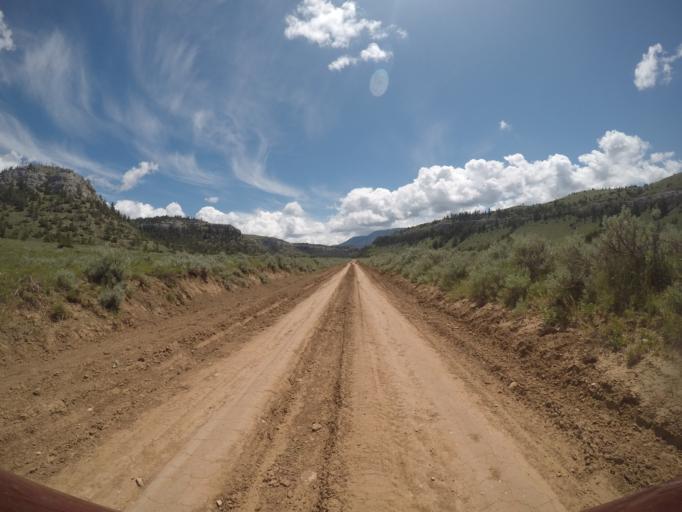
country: US
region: Wyoming
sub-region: Big Horn County
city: Lovell
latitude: 45.2339
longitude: -108.6159
